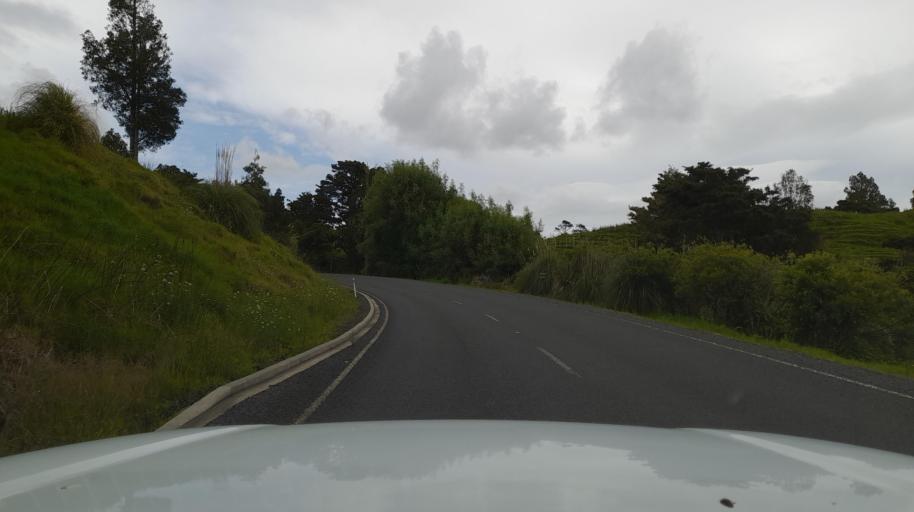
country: NZ
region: Northland
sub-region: Far North District
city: Kaitaia
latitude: -35.3059
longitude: 173.3448
